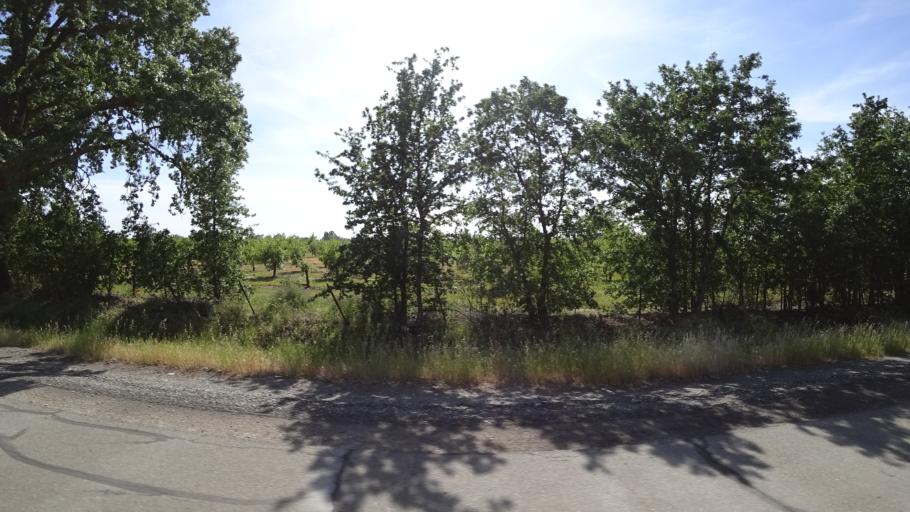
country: US
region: California
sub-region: Tehama County
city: Los Molinos
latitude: 39.9562
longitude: -122.0594
